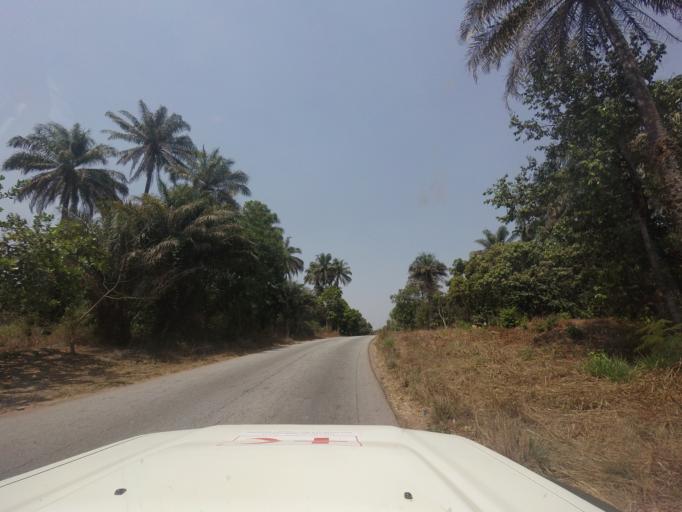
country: GN
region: Kindia
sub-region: Kindia
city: Kindia
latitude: 9.9395
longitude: -12.9748
